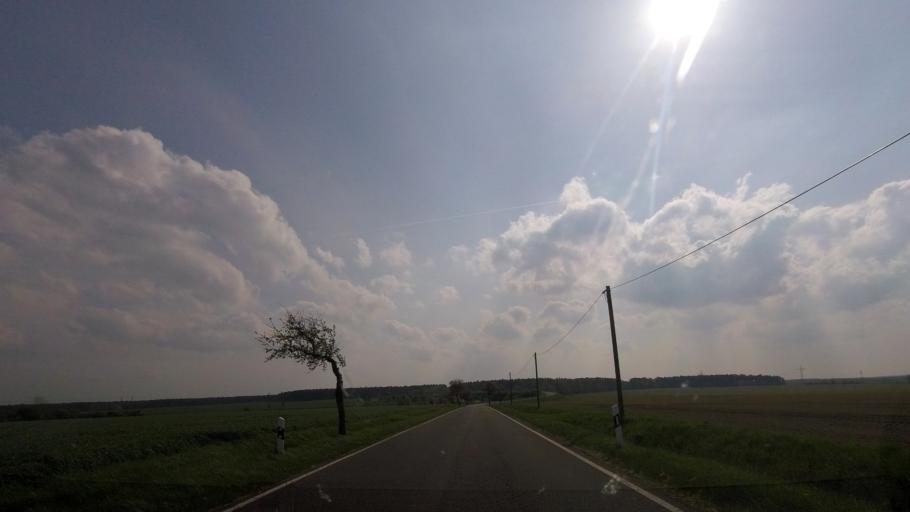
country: DE
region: Saxony-Anhalt
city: Zahna
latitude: 51.9453
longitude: 12.8384
